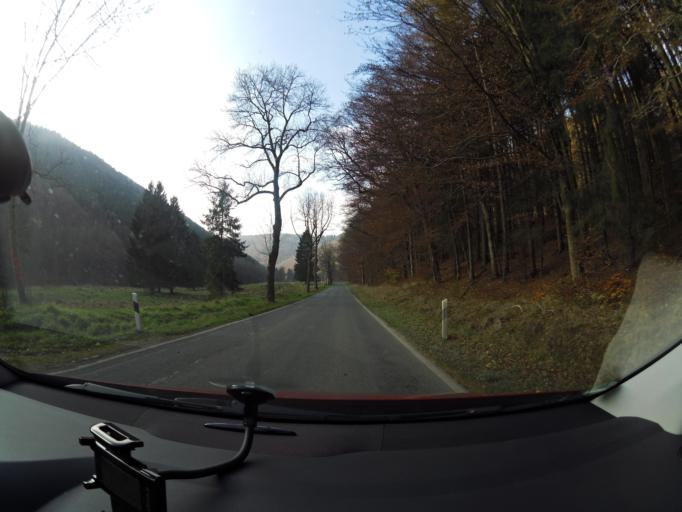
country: DE
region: Lower Saxony
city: Herzberg am Harz
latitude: 51.6794
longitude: 10.3887
